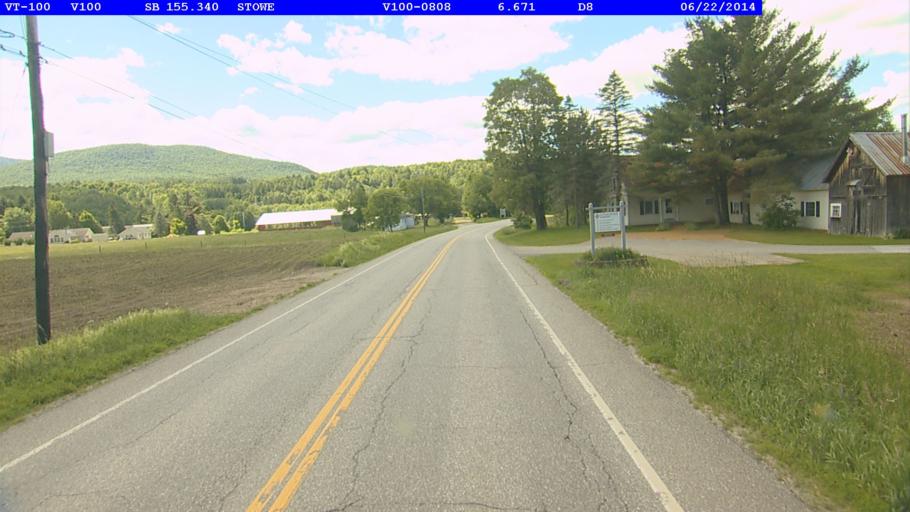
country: US
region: Vermont
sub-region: Lamoille County
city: Morristown
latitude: 44.4930
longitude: -72.6370
